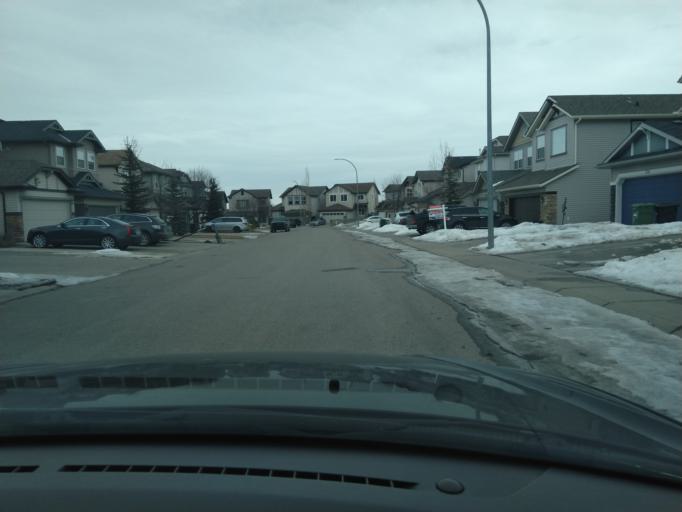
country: CA
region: Alberta
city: Calgary
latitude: 51.1574
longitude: -114.0891
